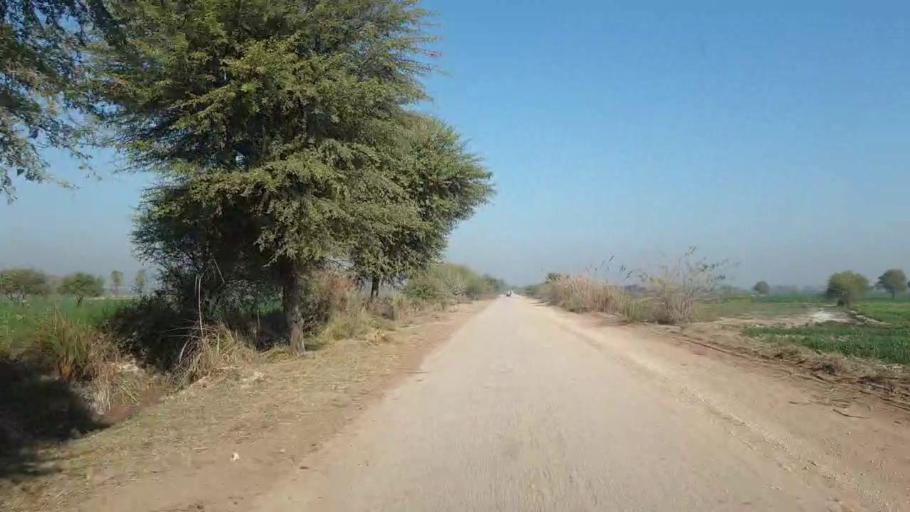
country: PK
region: Sindh
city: Shahdadpur
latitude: 25.9271
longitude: 68.5060
